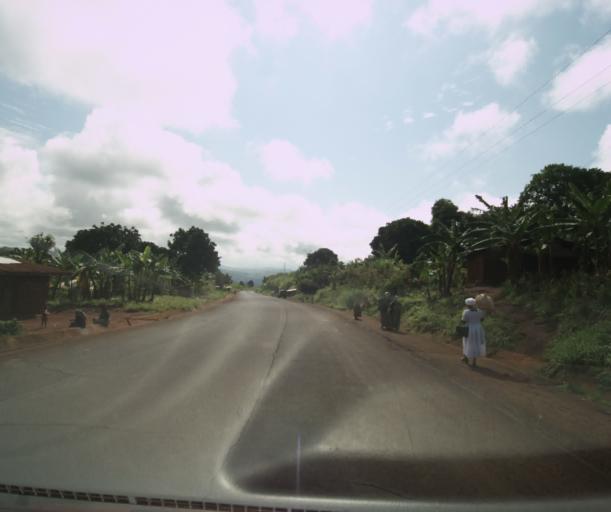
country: CM
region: West
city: Bafoussam
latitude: 5.4820
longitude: 10.4855
